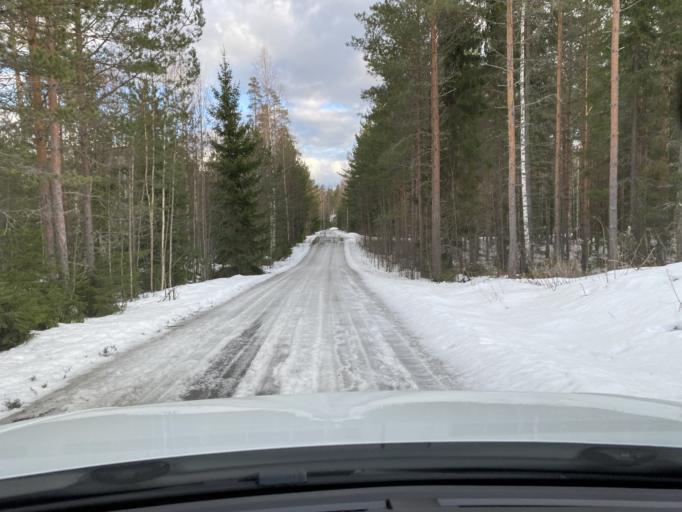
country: FI
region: Pirkanmaa
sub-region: Lounais-Pirkanmaa
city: Mouhijaervi
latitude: 61.4337
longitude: 22.9861
